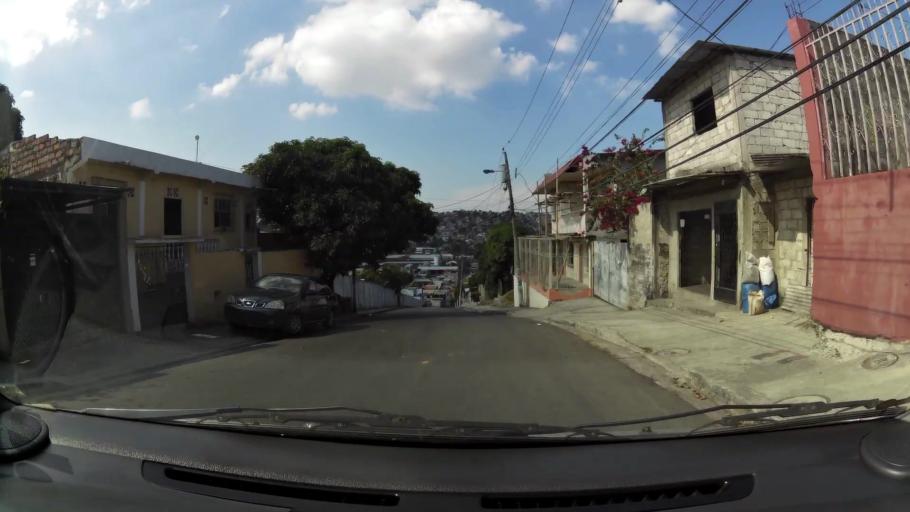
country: EC
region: Guayas
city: Guayaquil
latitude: -2.1538
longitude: -79.9372
